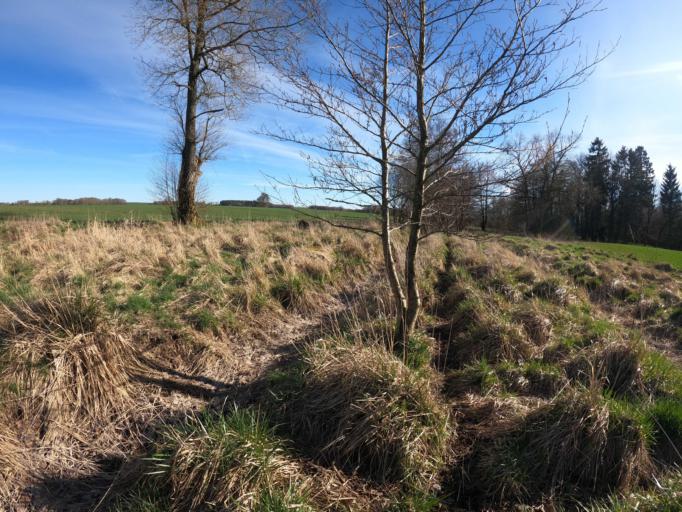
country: PL
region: West Pomeranian Voivodeship
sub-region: Powiat gryficki
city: Brojce
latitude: 53.9139
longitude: 15.3226
